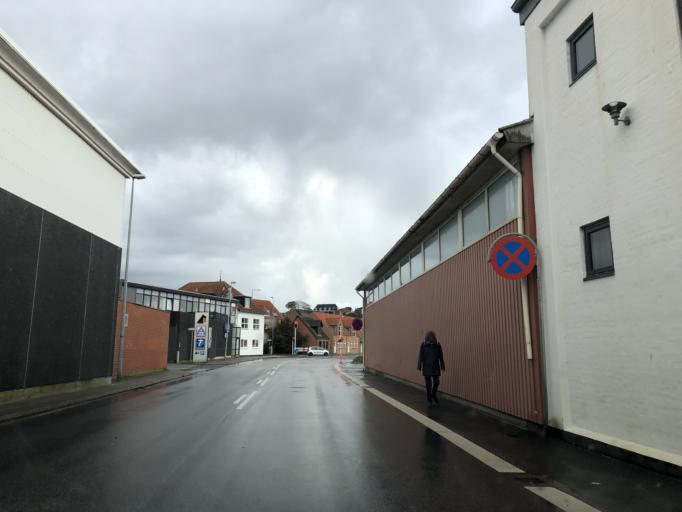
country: DK
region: Central Jutland
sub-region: Lemvig Kommune
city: Lemvig
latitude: 56.5522
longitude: 8.3103
